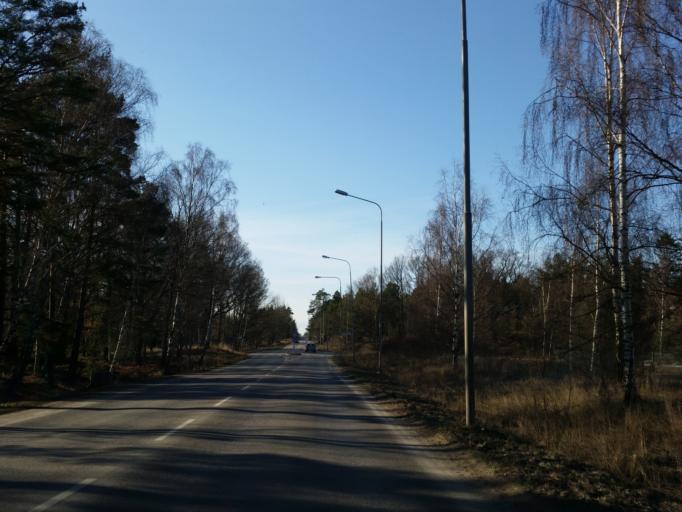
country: SE
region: Kalmar
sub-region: Oskarshamns Kommun
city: Oskarshamn
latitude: 57.2524
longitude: 16.4454
